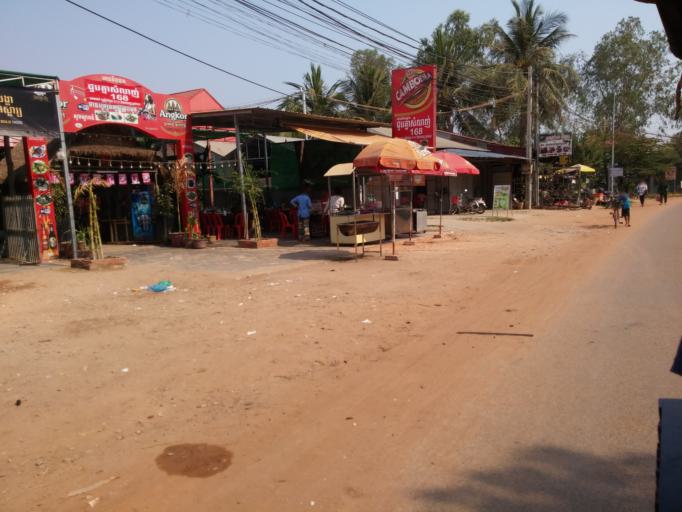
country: KH
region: Siem Reap
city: Siem Reap
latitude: 13.3768
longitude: 103.8511
